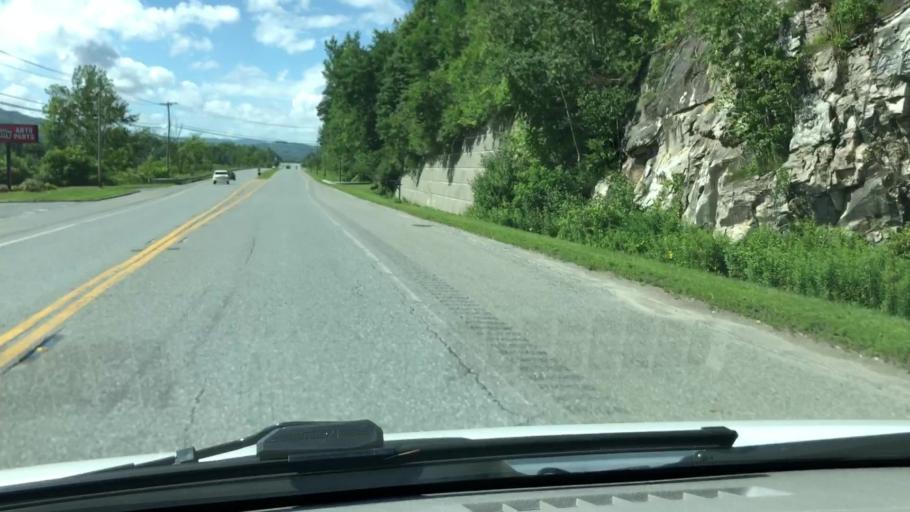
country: US
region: Massachusetts
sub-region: Berkshire County
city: North Adams
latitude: 42.6771
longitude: -73.1073
